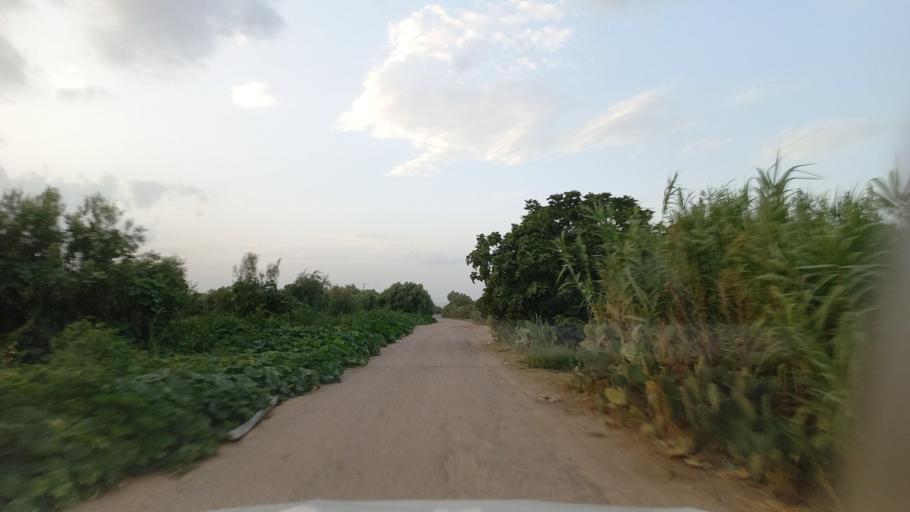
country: TN
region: Al Qasrayn
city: Kasserine
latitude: 35.2757
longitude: 9.0526
